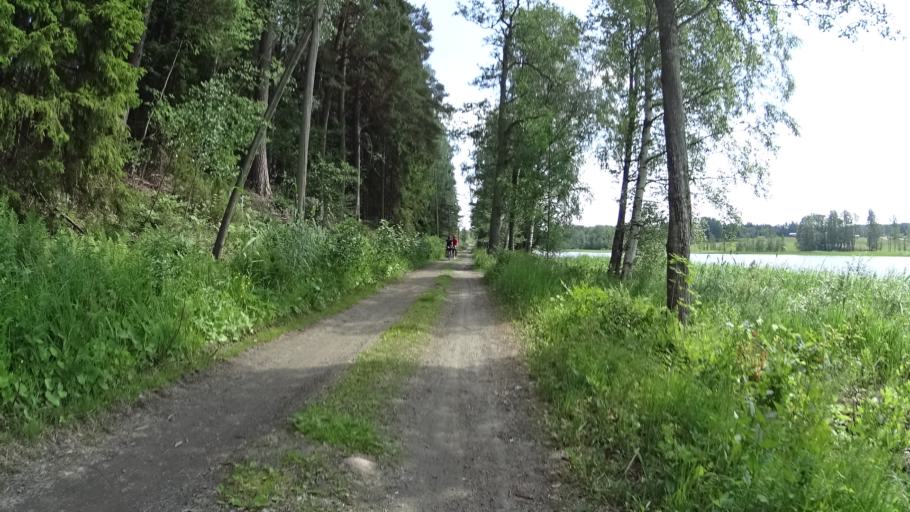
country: FI
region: Uusimaa
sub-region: Raaseporin
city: Pohja
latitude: 60.1139
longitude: 23.5432
